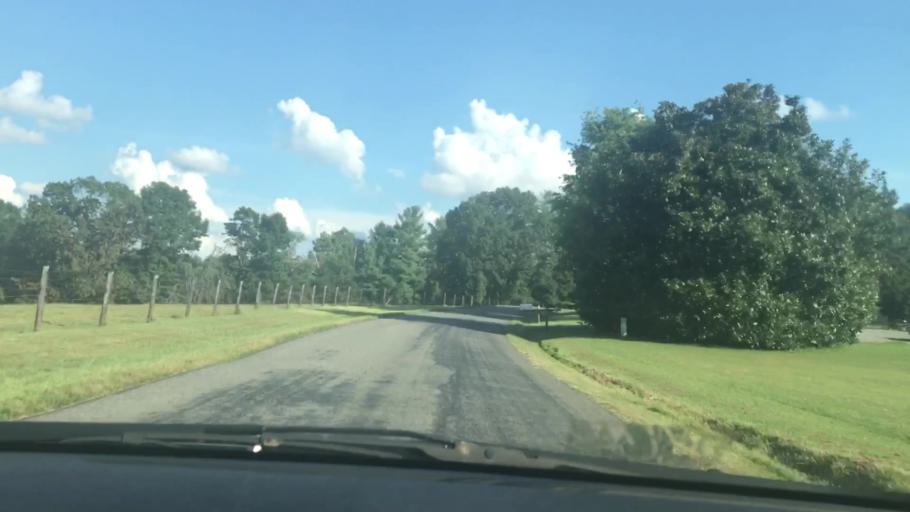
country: US
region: Virginia
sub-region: Henrico County
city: Short Pump
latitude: 37.6718
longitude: -77.7137
